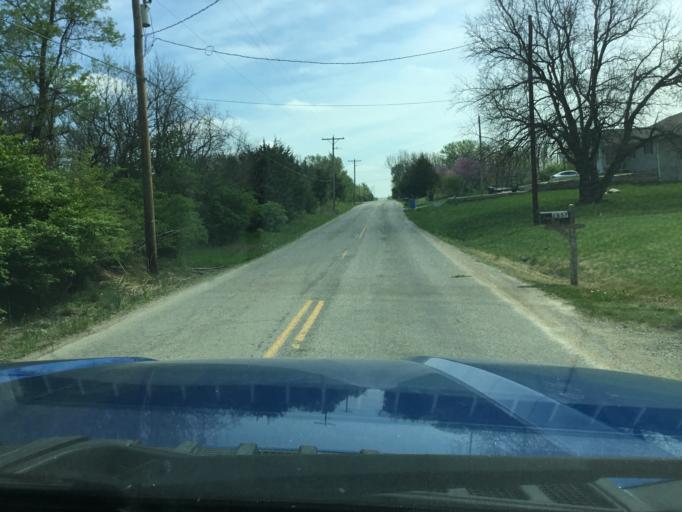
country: US
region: Kansas
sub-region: Shawnee County
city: Topeka
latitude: 39.1170
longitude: -95.5886
